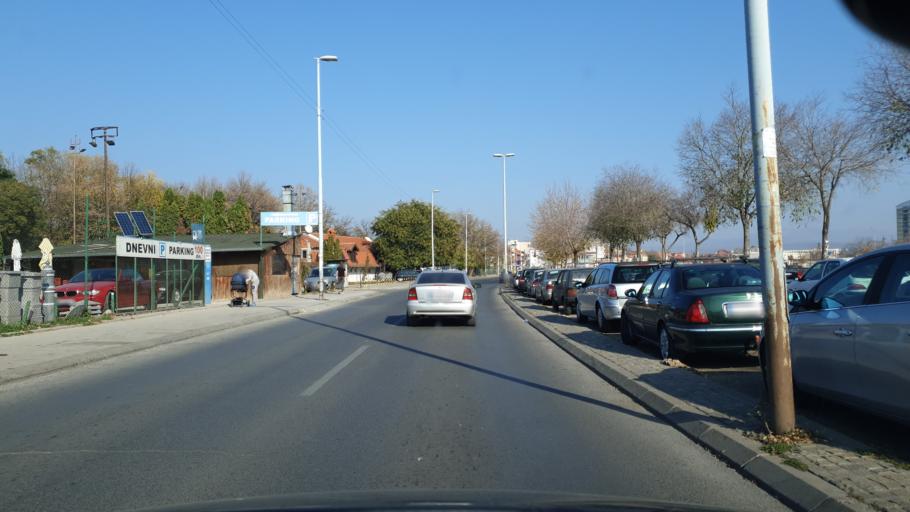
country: RS
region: Central Serbia
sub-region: Nisavski Okrug
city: Nis
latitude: 43.3256
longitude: 21.8992
